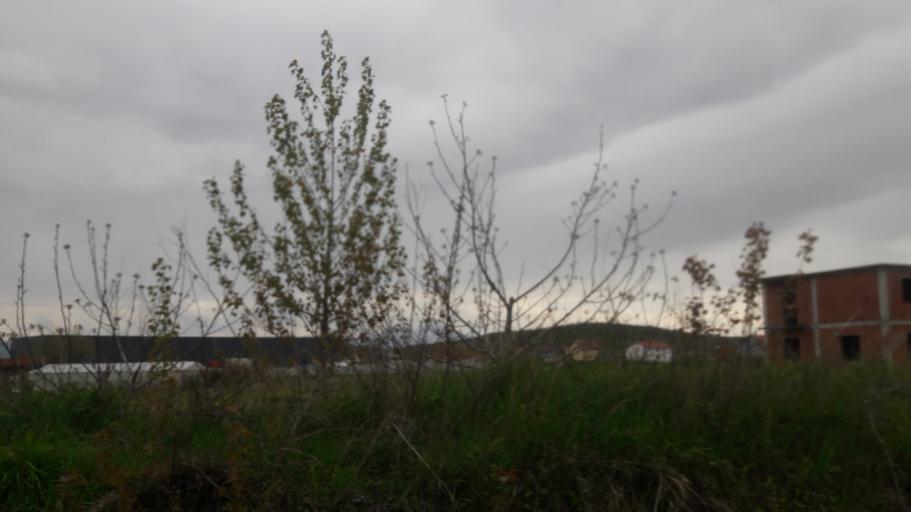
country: AL
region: Shkoder
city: Vukatane
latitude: 41.9714
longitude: 19.5403
